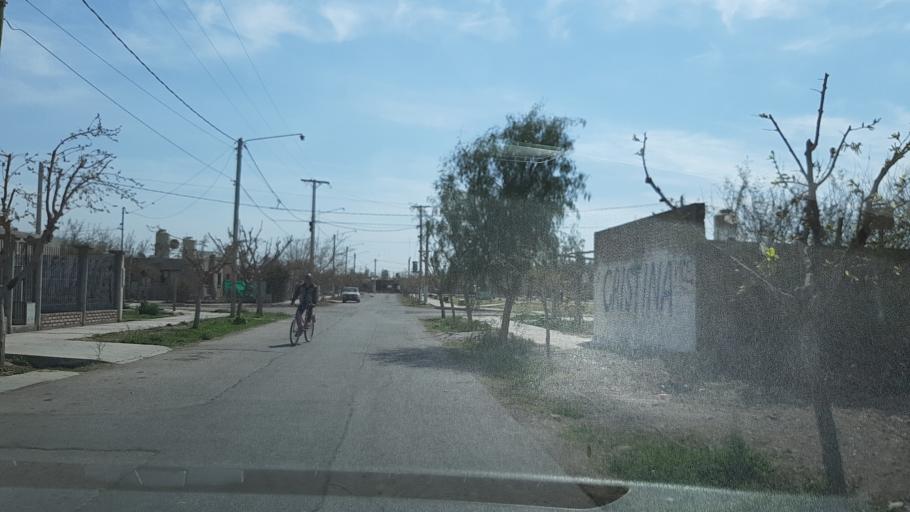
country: AR
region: San Juan
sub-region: Departamento de Zonda
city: Zonda
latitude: -31.5417
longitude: -68.7508
